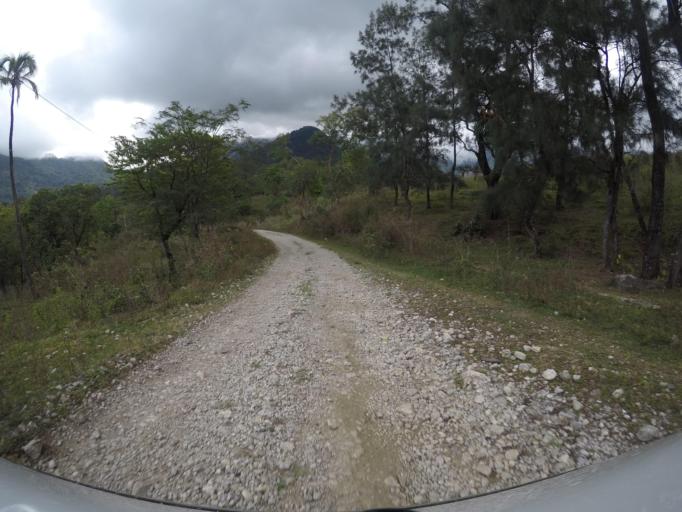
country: TL
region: Baucau
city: Venilale
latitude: -8.6715
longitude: 126.6339
